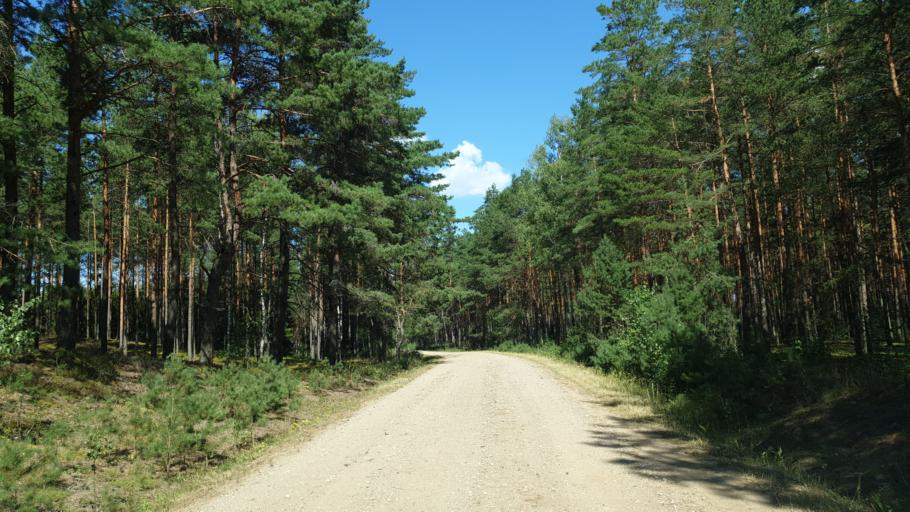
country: LT
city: Sirvintos
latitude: 54.8932
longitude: 24.9568
